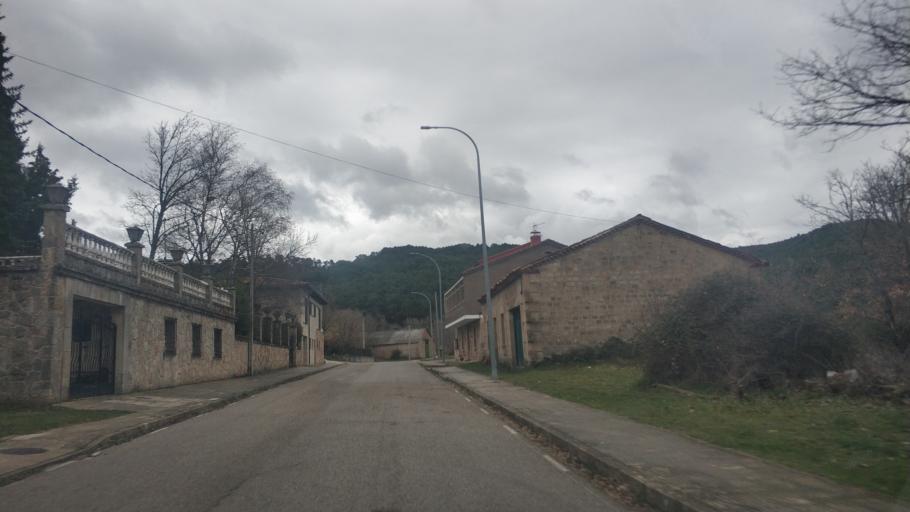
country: ES
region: Castille and Leon
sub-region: Provincia de Burgos
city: Canicosa de la Sierra
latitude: 41.9349
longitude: -3.0380
